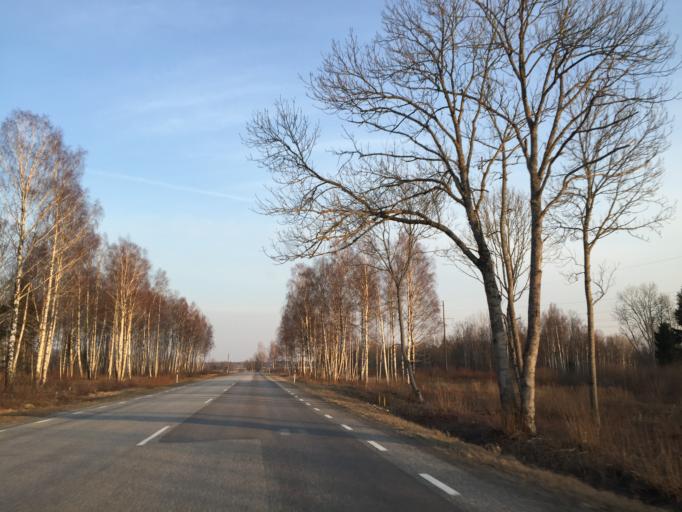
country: EE
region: Laeaene
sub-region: Lihula vald
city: Lihula
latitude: 58.5417
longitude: 24.0069
